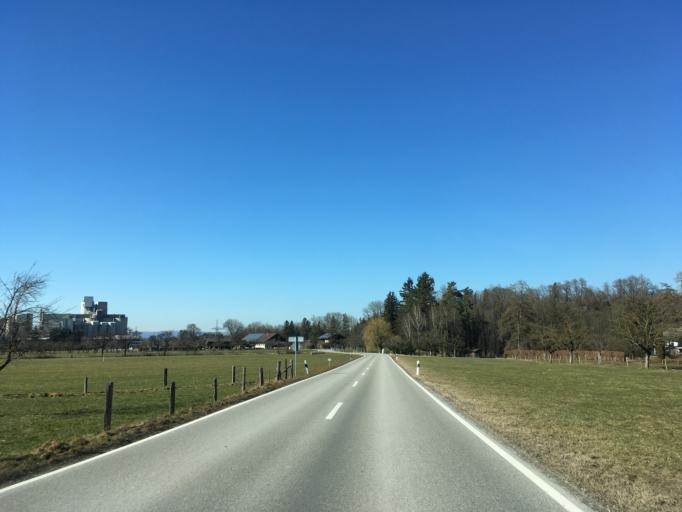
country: DE
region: Bavaria
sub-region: Upper Bavaria
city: Samerberg
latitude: 47.7919
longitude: 12.1923
